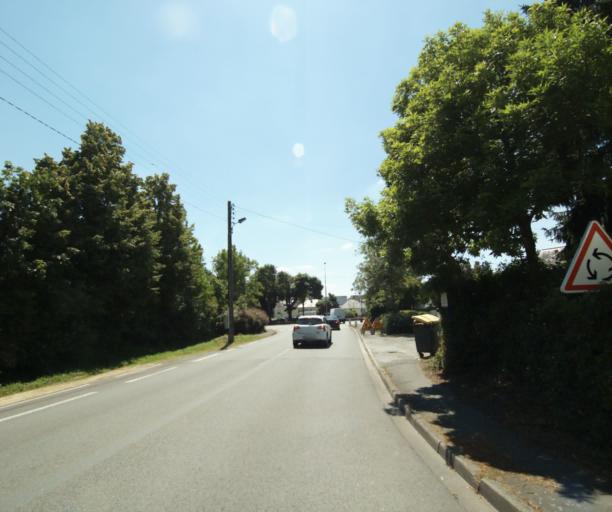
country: FR
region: Pays de la Loire
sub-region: Departement de la Mayenne
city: Laval
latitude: 48.0789
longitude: -0.7503
